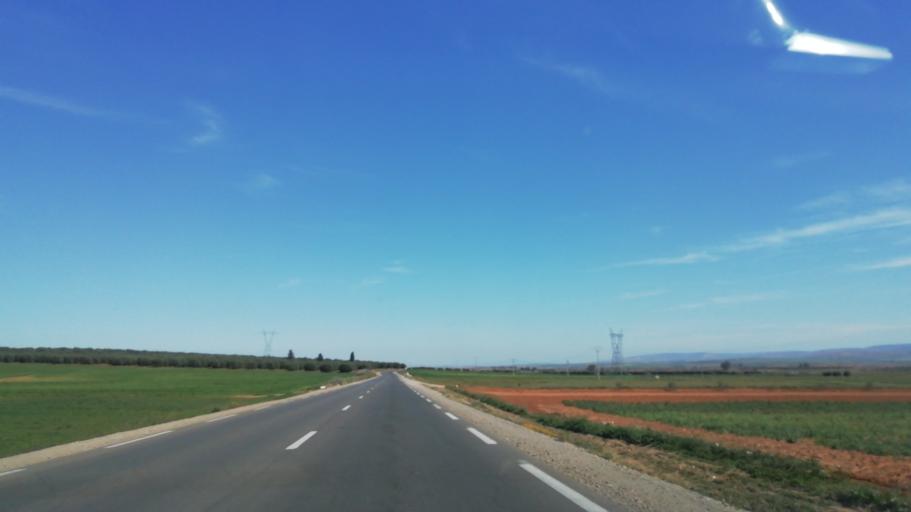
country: DZ
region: Mascara
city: Oued el Abtal
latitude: 35.4189
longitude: 0.4218
